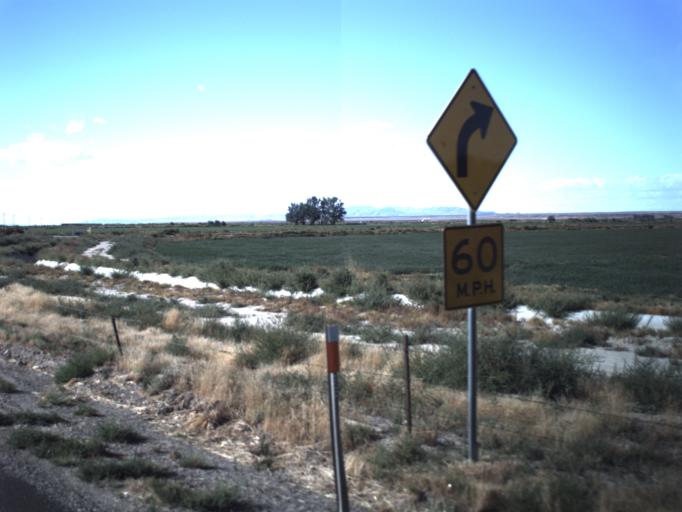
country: US
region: Utah
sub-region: Millard County
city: Delta
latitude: 39.2592
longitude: -112.6532
